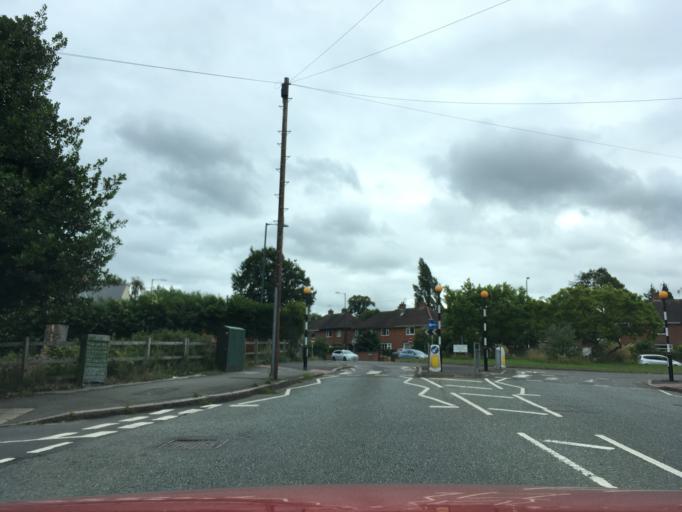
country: GB
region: England
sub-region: Nottinghamshire
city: Arnold
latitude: 52.9855
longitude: -1.1475
